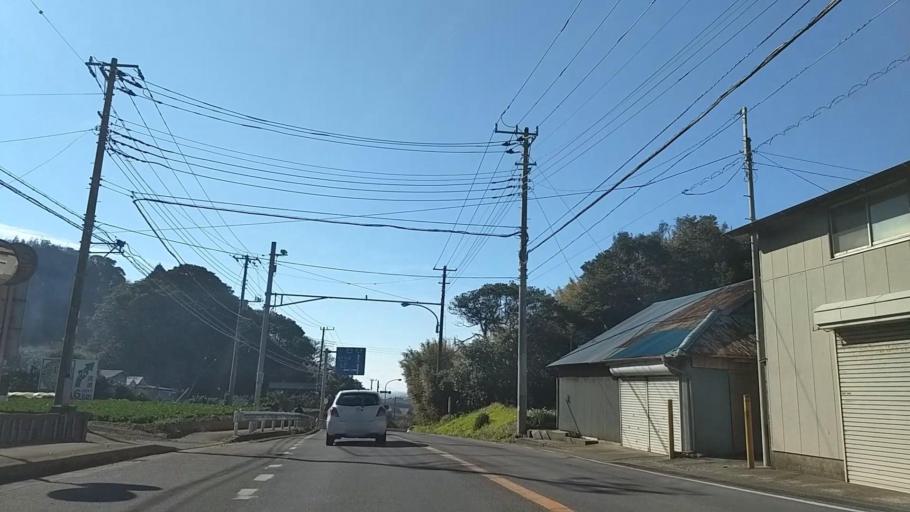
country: JP
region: Chiba
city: Asahi
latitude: 35.7005
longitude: 140.7379
